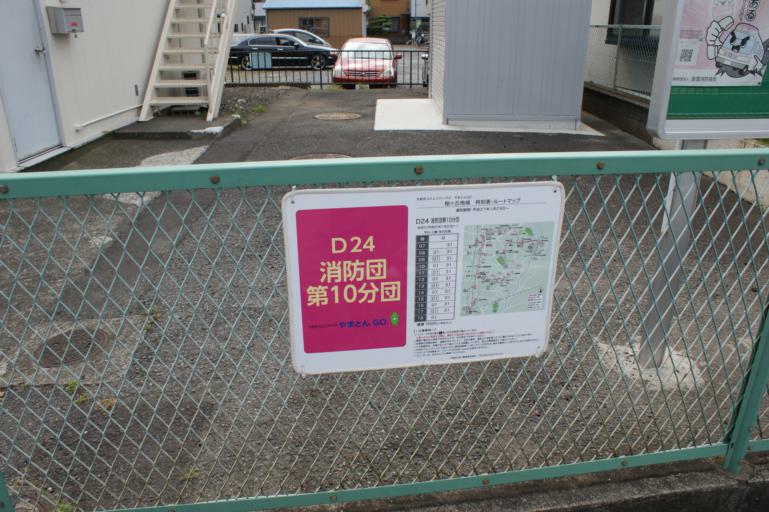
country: JP
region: Kanagawa
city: Minami-rinkan
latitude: 35.4510
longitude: 139.4675
